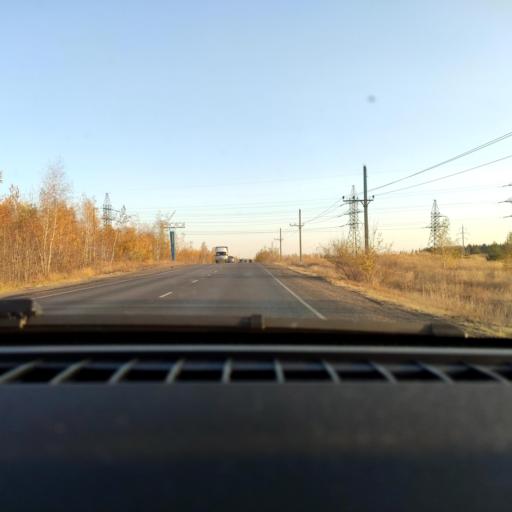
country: RU
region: Voronezj
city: Maslovka
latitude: 51.5821
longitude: 39.2604
